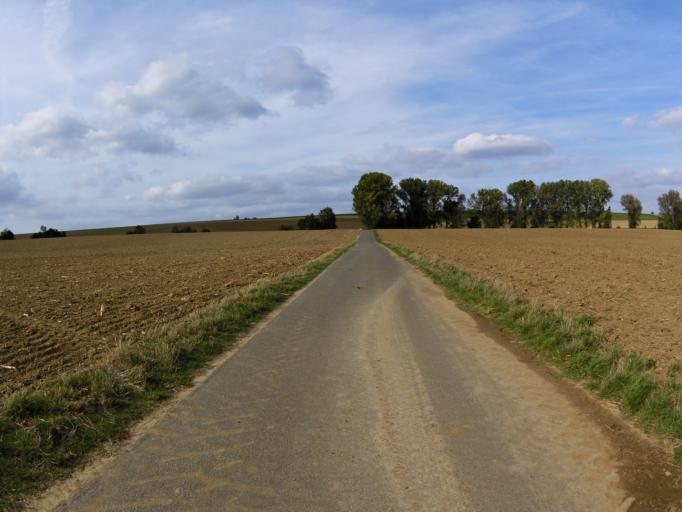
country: DE
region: Bavaria
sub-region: Regierungsbezirk Unterfranken
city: Reichenberg
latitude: 49.7053
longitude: 9.9494
